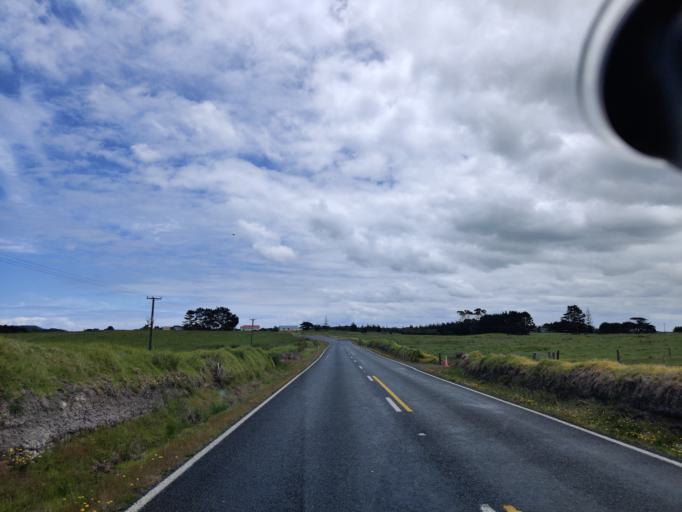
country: NZ
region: Northland
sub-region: Far North District
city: Kaitaia
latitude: -34.6753
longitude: 173.0004
